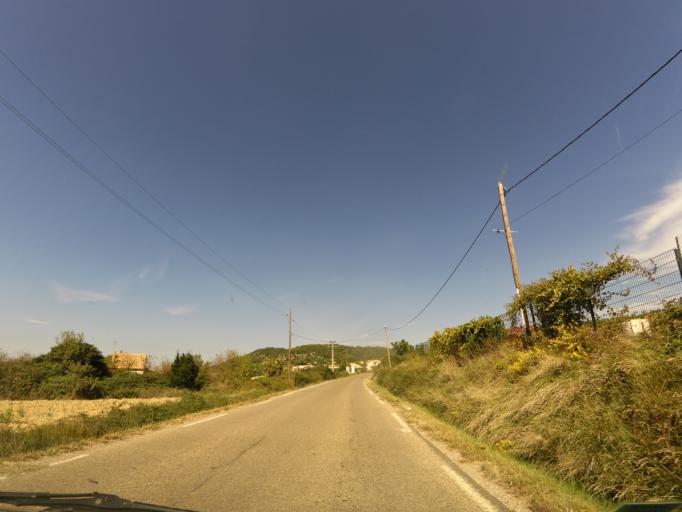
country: FR
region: Languedoc-Roussillon
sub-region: Departement du Gard
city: Nages-et-Solorgues
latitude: 43.7855
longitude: 4.2324
